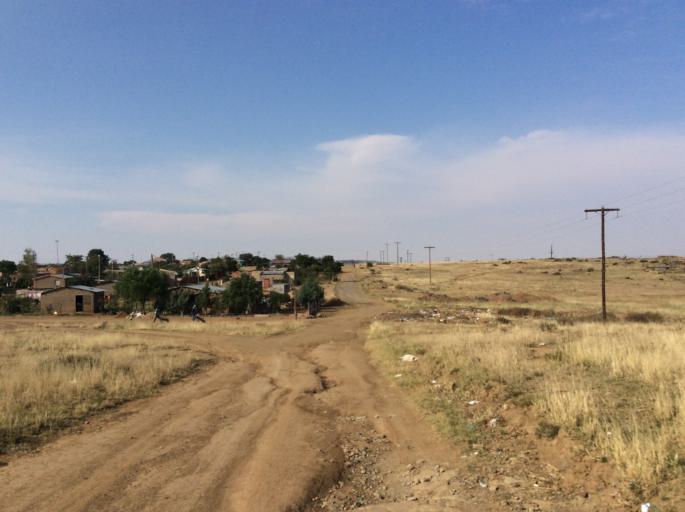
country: LS
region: Mafeteng
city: Mafeteng
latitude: -29.7170
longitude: 27.0109
